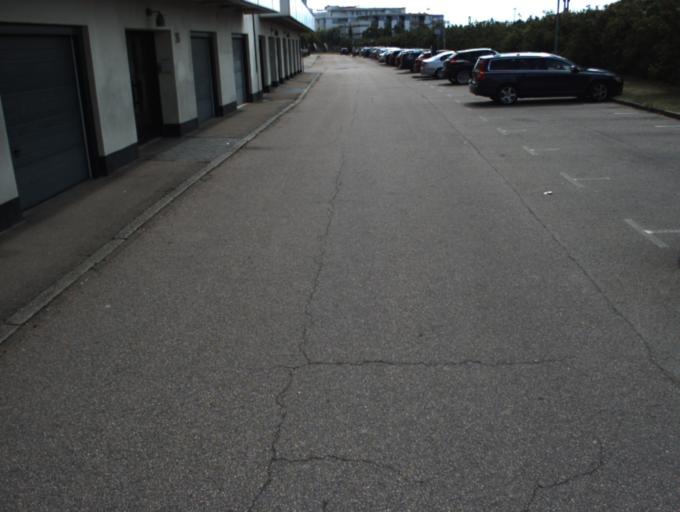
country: SE
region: Skane
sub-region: Helsingborg
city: Helsingborg
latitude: 56.0537
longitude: 12.6845
